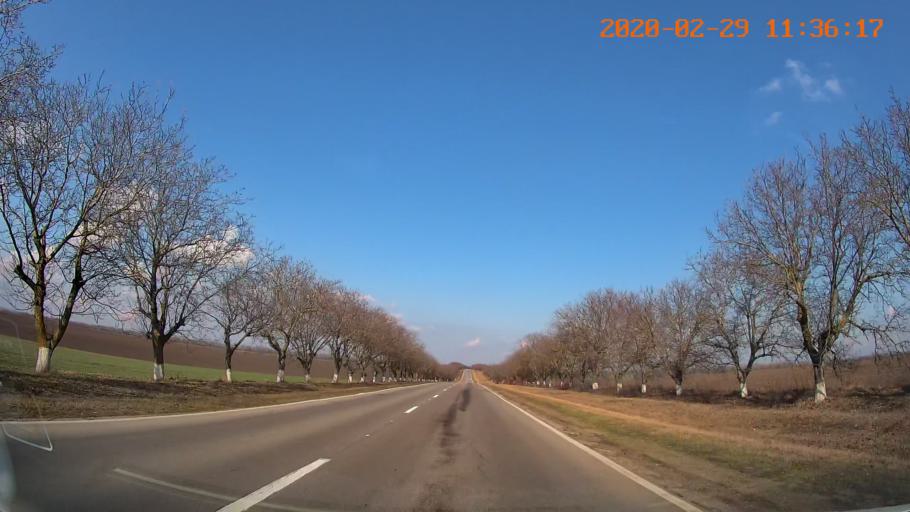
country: MD
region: Rezina
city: Saharna
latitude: 47.5937
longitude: 29.0573
